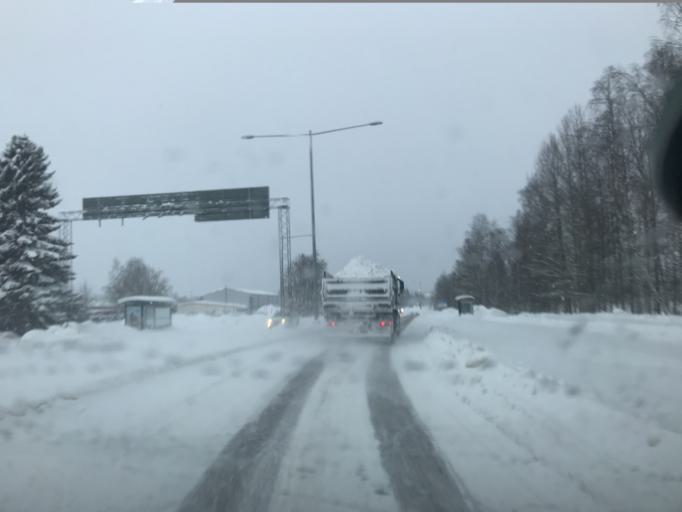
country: SE
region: Norrbotten
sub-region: Lulea Kommun
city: Lulea
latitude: 65.6131
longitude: 22.1342
